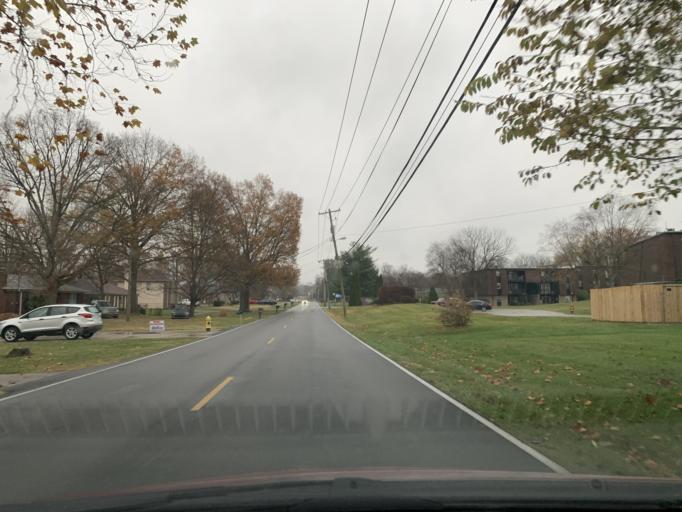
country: US
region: Kentucky
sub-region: Jefferson County
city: Buechel
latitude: 38.1978
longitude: -85.6318
